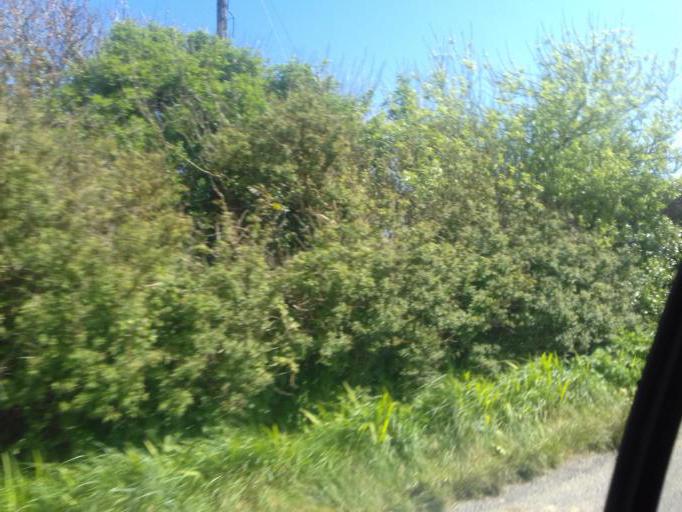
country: IE
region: Munster
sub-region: Waterford
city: Dunmore East
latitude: 52.1643
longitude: -6.8936
